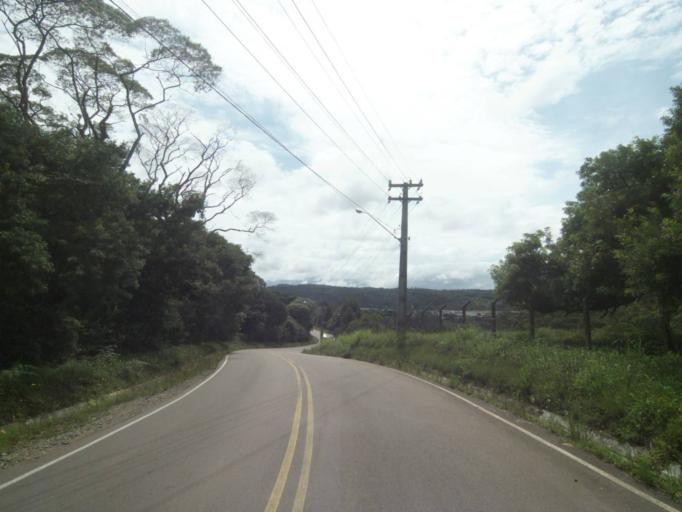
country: BR
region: Parana
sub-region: Campina Grande Do Sul
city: Campina Grande do Sul
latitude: -25.3156
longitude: -49.0270
